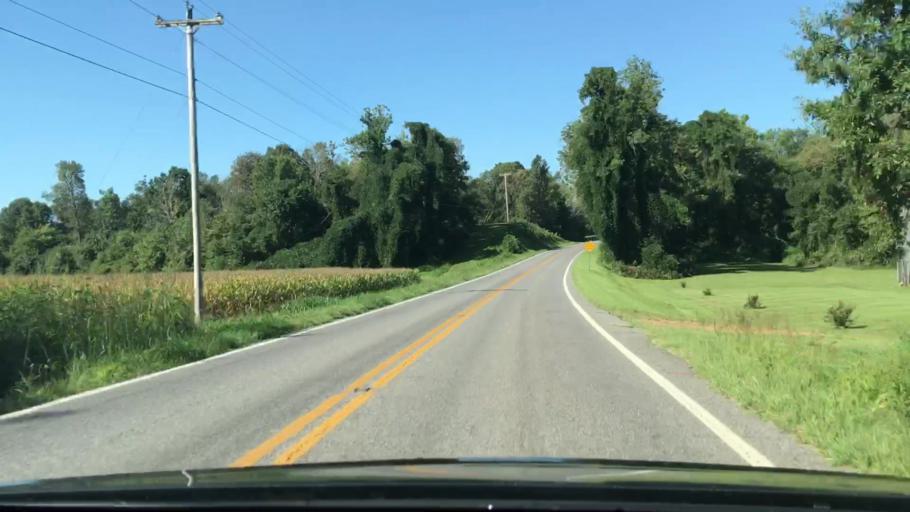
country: US
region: Kentucky
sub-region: Graves County
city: Mayfield
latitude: 36.7676
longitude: -88.5660
